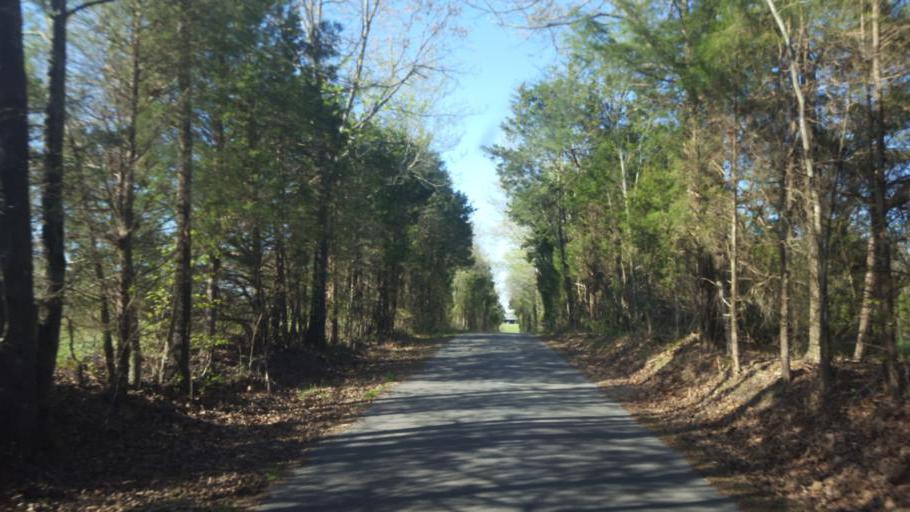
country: US
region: Kentucky
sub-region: Barren County
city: Cave City
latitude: 37.1769
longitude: -85.9972
